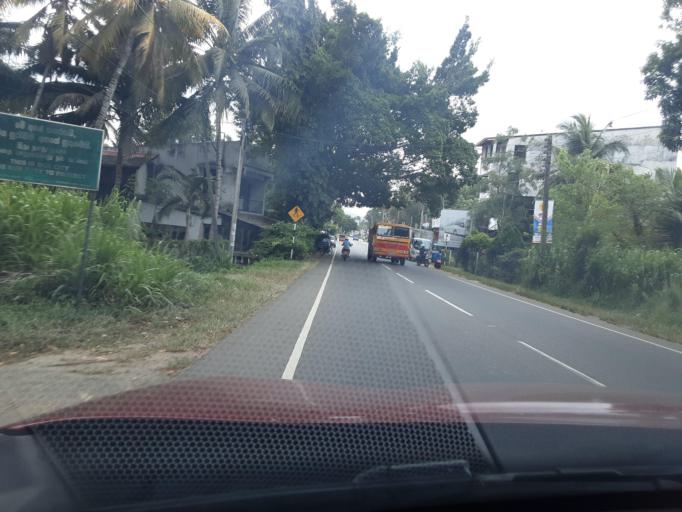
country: LK
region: North Western
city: Kurunegala
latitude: 7.4373
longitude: 80.2085
